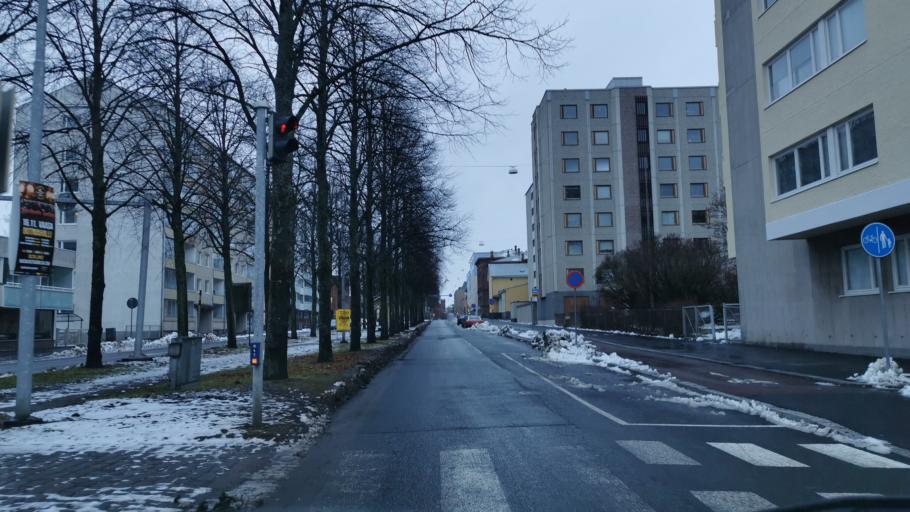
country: FI
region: Ostrobothnia
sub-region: Vaasa
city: Vaasa
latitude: 63.0997
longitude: 21.6056
